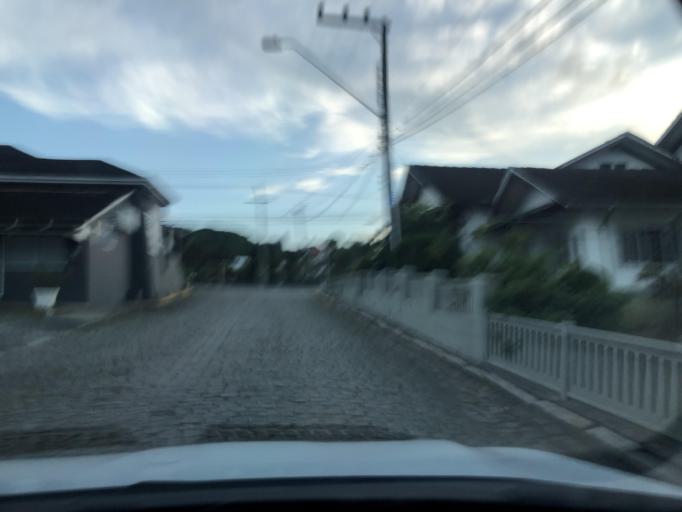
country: BR
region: Santa Catarina
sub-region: Joinville
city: Joinville
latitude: -26.2962
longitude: -48.8635
